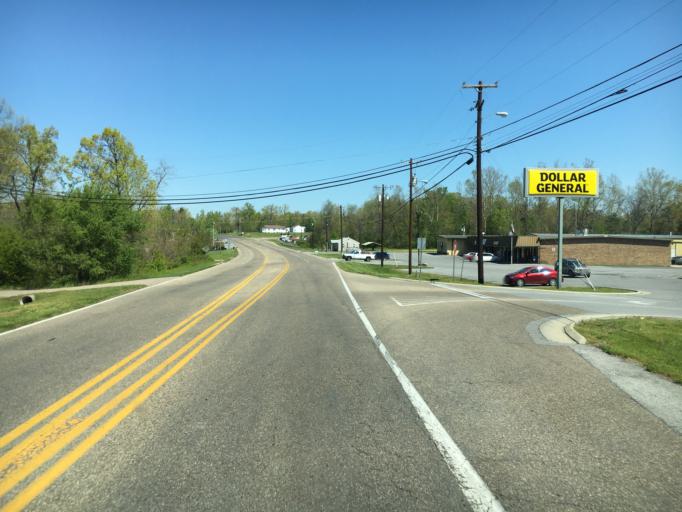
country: US
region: Virginia
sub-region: Augusta County
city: Crimora
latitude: 38.1510
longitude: -78.8411
